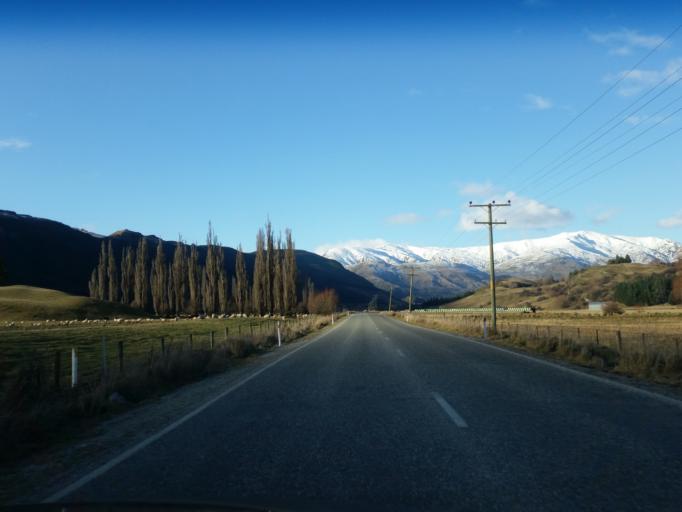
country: NZ
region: Otago
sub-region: Queenstown-Lakes District
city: Arrowtown
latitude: -44.9528
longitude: 168.7466
